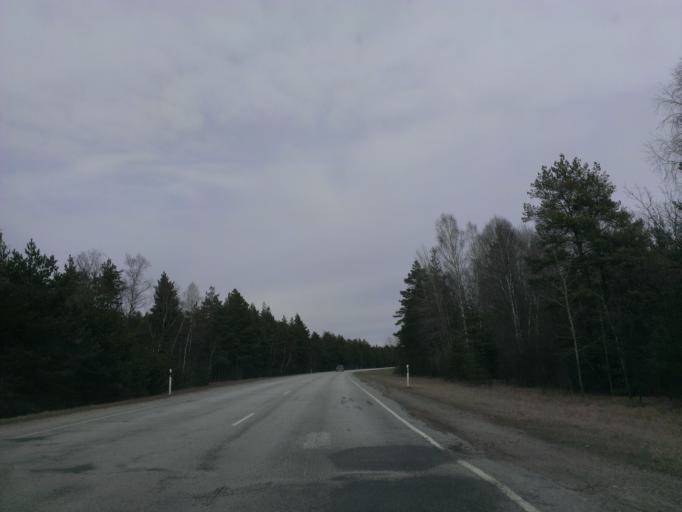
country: EE
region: Laeaene
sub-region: Lihula vald
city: Lihula
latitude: 58.6043
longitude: 23.5567
